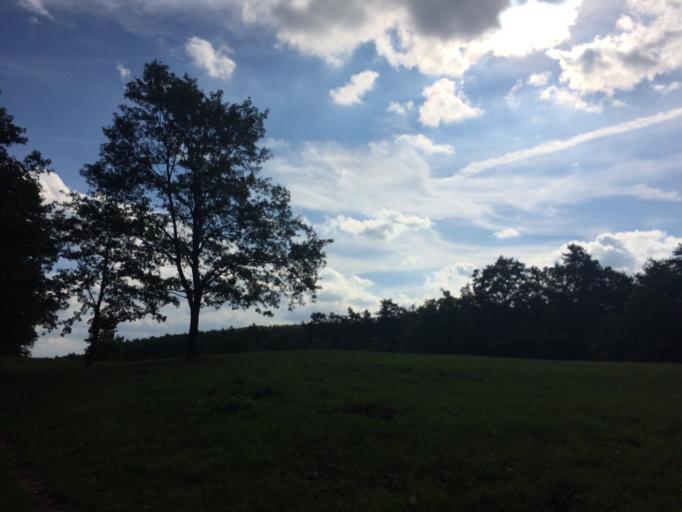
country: HU
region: Pest
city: Nagymaros
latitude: 47.8005
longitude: 18.9432
